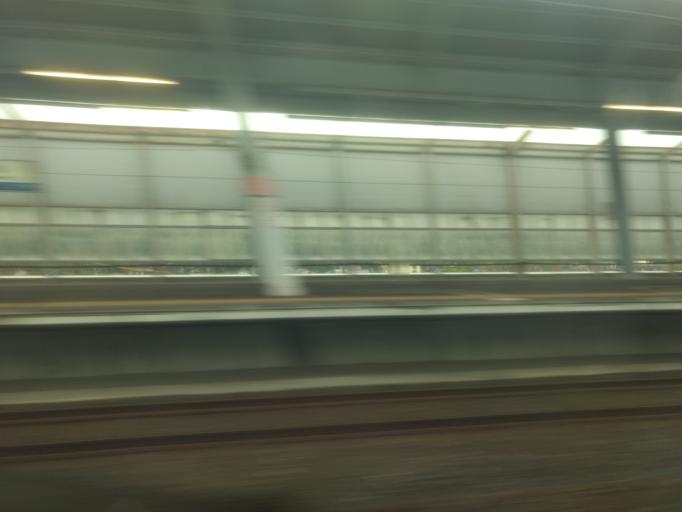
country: JP
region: Yamaguchi
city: Iwakuni
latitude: 34.1634
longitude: 132.1490
